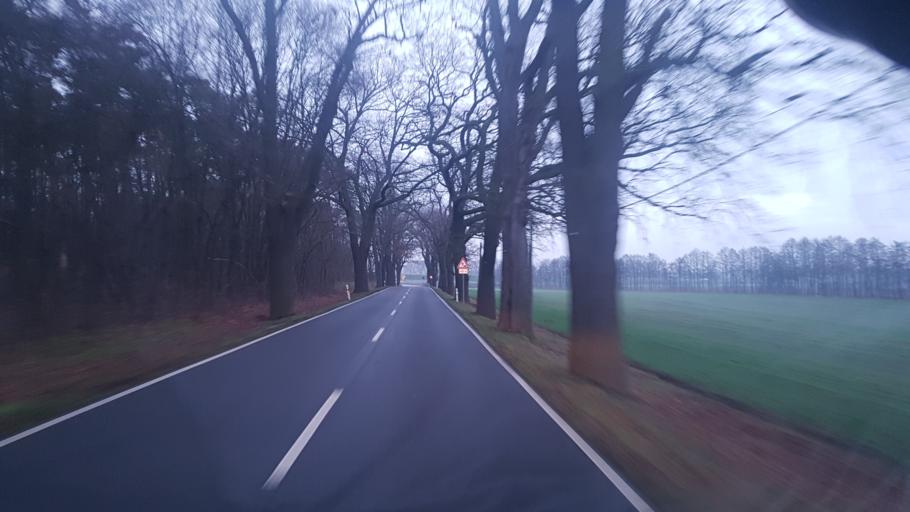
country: DE
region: Brandenburg
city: Trebbin
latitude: 52.2407
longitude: 13.2227
